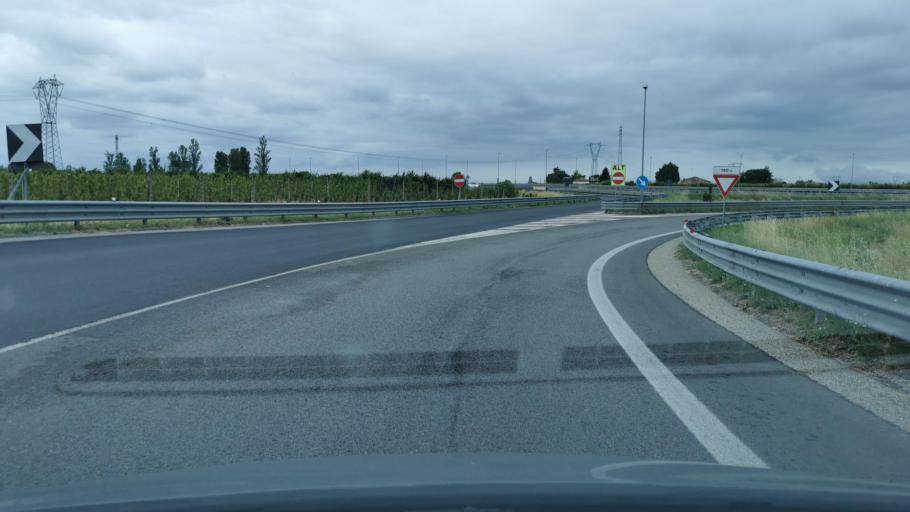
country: IT
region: Emilia-Romagna
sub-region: Provincia di Ravenna
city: Bagnacavallo
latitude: 44.4005
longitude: 11.9684
